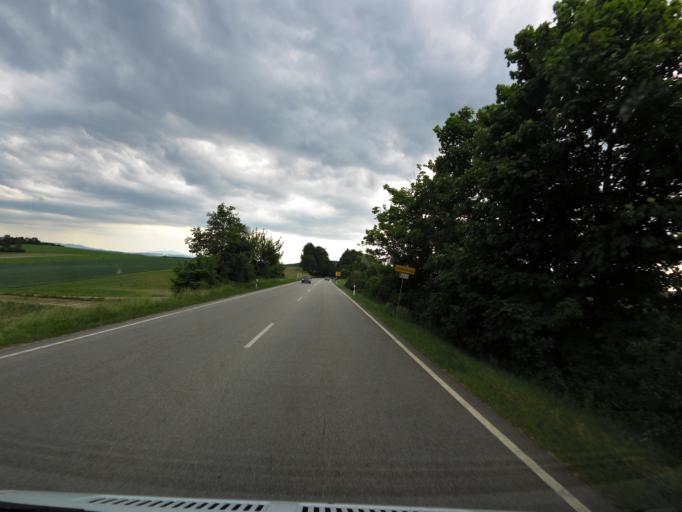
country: DE
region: Bavaria
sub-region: Lower Bavaria
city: Buchlberg
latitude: 48.6954
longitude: 13.5094
